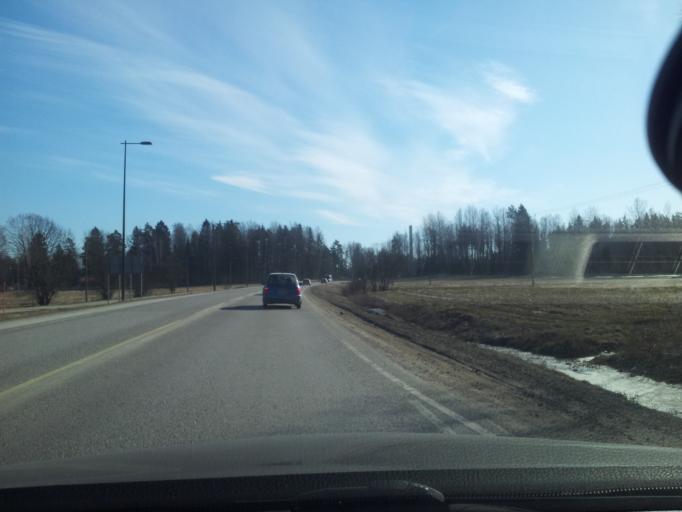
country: FI
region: Uusimaa
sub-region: Helsinki
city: Espoo
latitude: 60.1674
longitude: 24.6231
